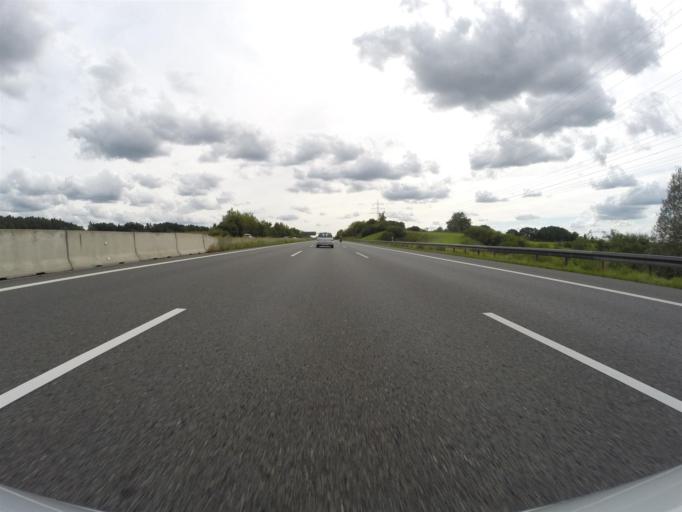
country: DE
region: Bavaria
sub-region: Regierungsbezirk Mittelfranken
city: Lauf an der Pegnitz
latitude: 49.4939
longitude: 11.2797
